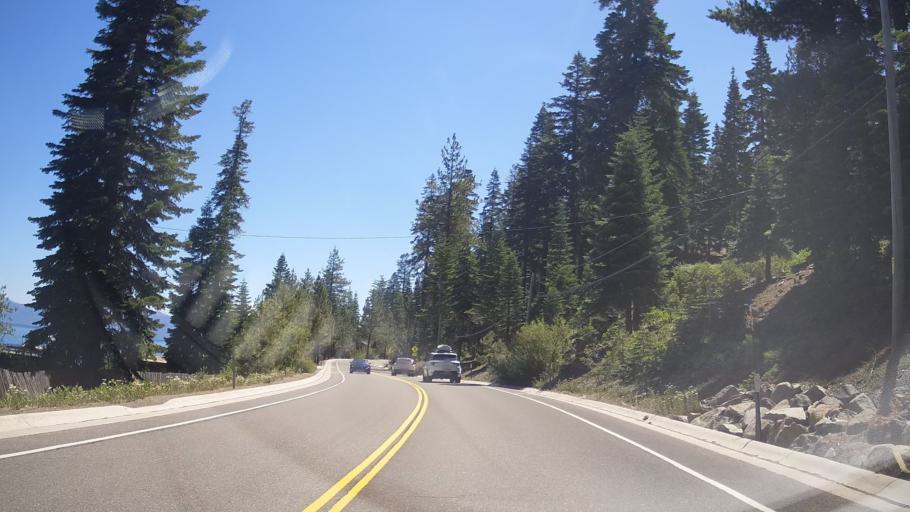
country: US
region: California
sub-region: Placer County
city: Tahoma
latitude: 39.0746
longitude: -120.1492
